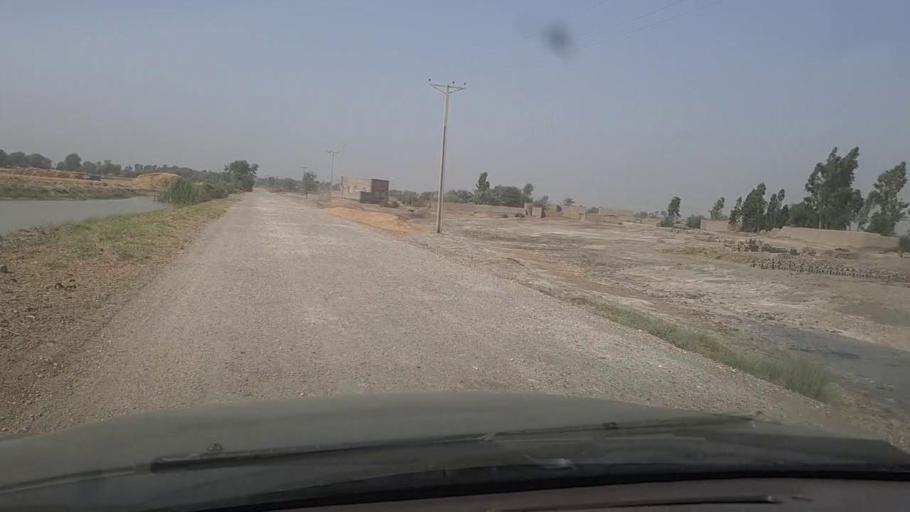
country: PK
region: Sindh
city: Garhi Yasin
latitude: 27.8780
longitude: 68.5657
